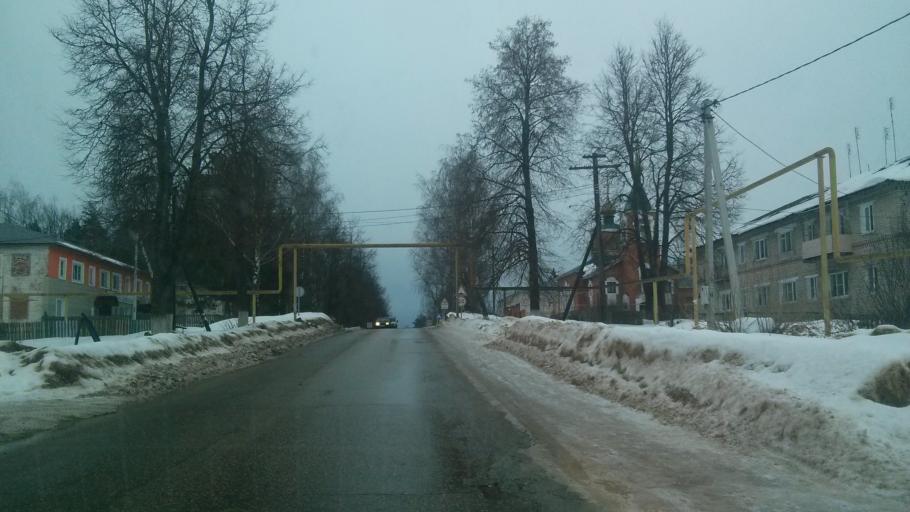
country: RU
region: Nizjnij Novgorod
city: Vacha
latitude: 55.7635
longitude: 42.5007
